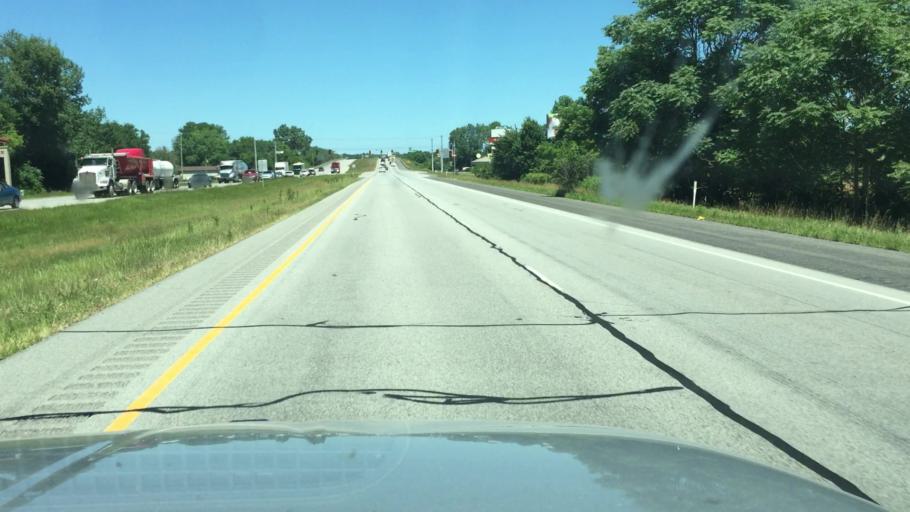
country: US
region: Indiana
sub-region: Porter County
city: Chesterton
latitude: 41.6043
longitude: -87.0426
